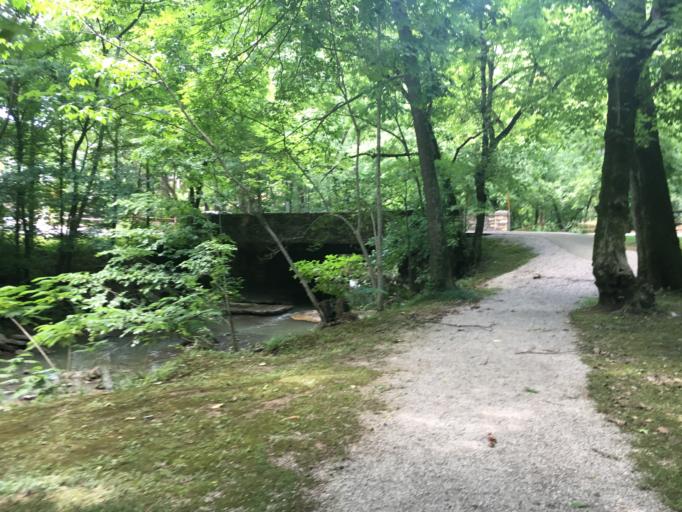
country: US
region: Alabama
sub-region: Jefferson County
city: Mountain Brook
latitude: 33.4760
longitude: -86.7633
